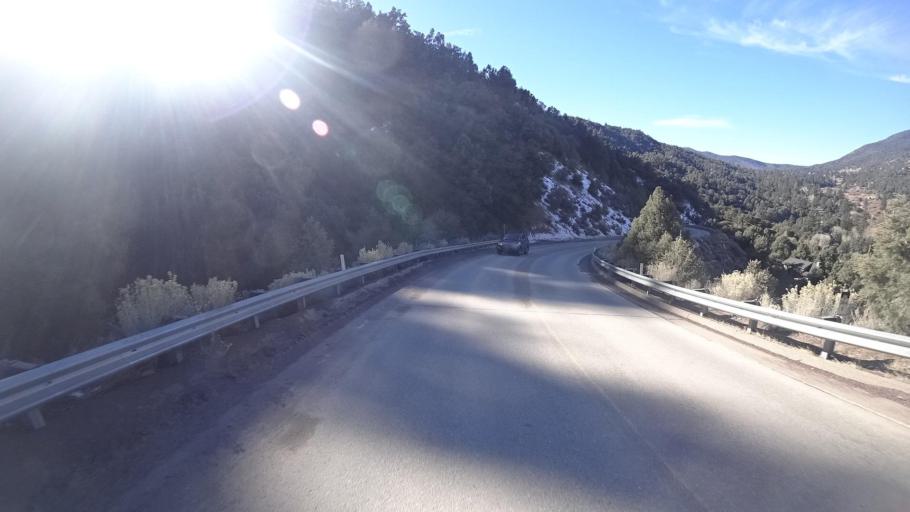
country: US
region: California
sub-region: Kern County
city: Pine Mountain Club
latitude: 34.8515
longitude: -119.1402
